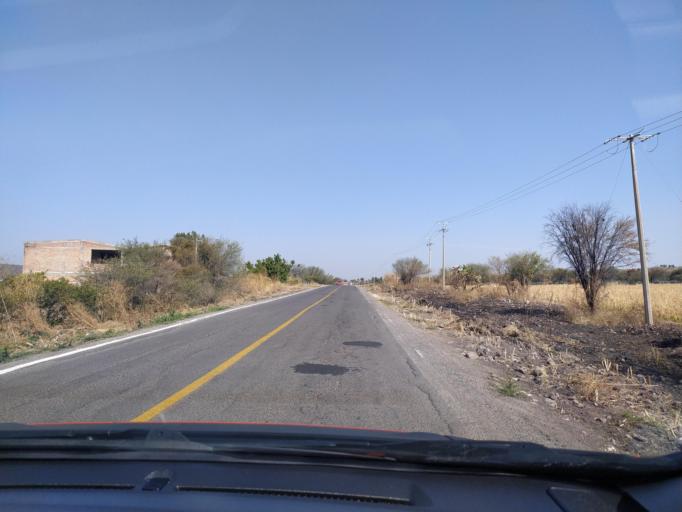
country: MX
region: Guanajuato
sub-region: San Francisco del Rincon
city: San Ignacio de Hidalgo
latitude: 20.8121
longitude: -101.8388
